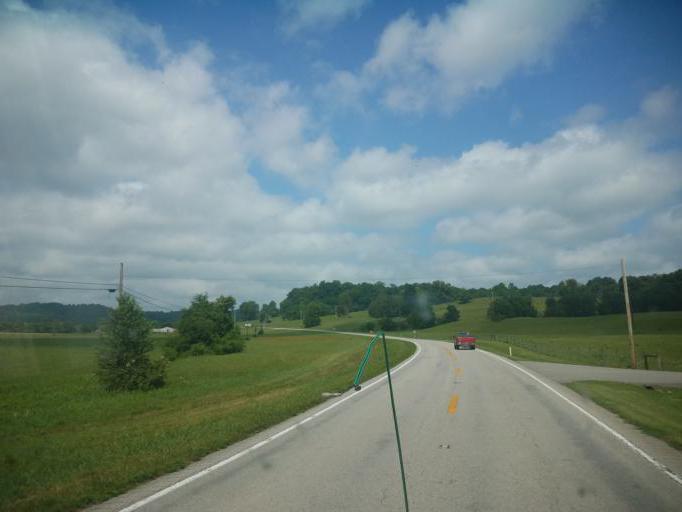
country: US
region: Kentucky
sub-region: Cumberland County
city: Burkesville
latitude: 36.8226
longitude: -85.4650
